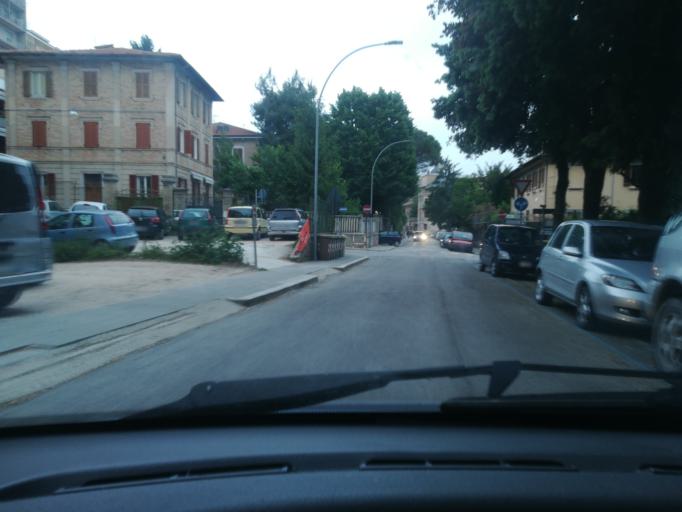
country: IT
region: The Marches
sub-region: Provincia di Macerata
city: Macerata
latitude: 43.3007
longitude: 13.4433
